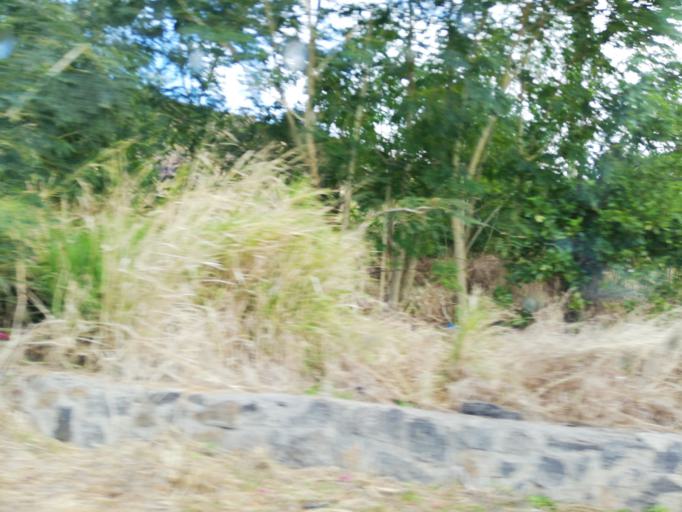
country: MU
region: Black River
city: Petite Riviere
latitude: -20.2041
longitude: 57.4638
